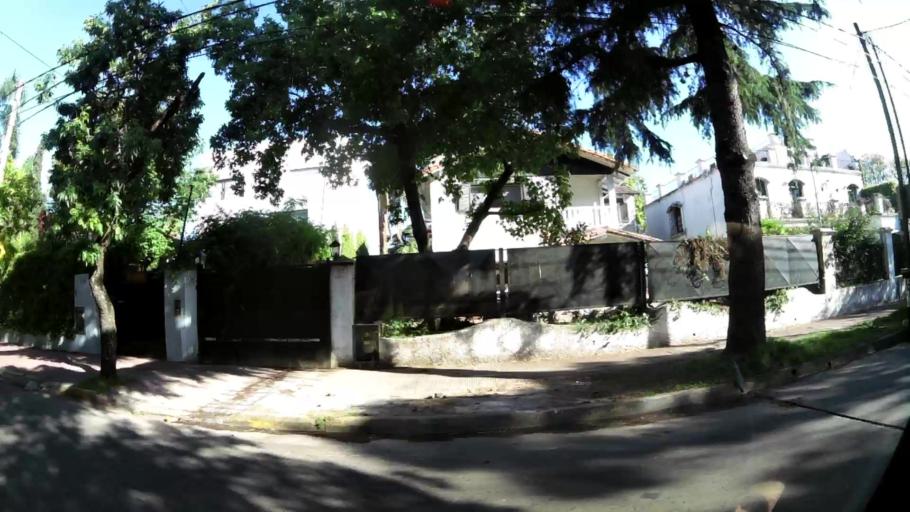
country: AR
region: Buenos Aires
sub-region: Partido de San Isidro
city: San Isidro
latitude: -34.4709
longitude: -58.5059
